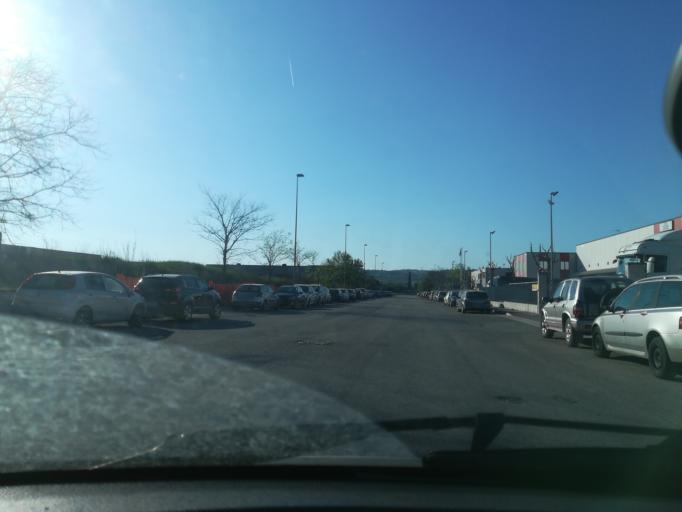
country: IT
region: The Marches
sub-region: Provincia di Macerata
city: Zona Industriale
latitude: 43.2627
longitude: 13.4844
